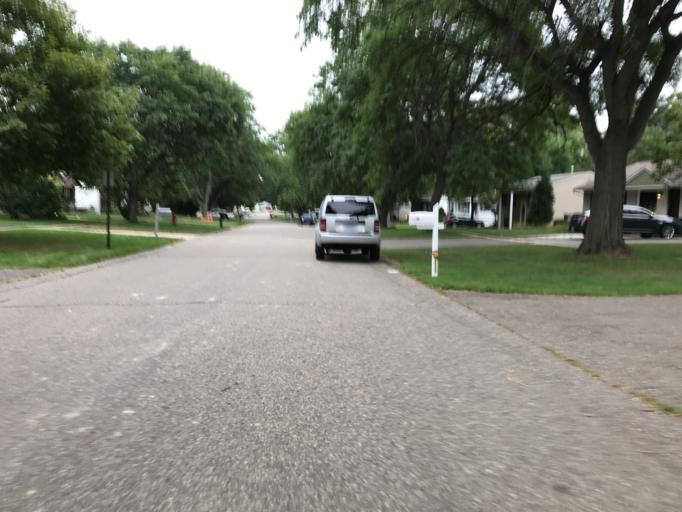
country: US
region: Michigan
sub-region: Oakland County
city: South Lyon
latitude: 42.4632
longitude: -83.6424
